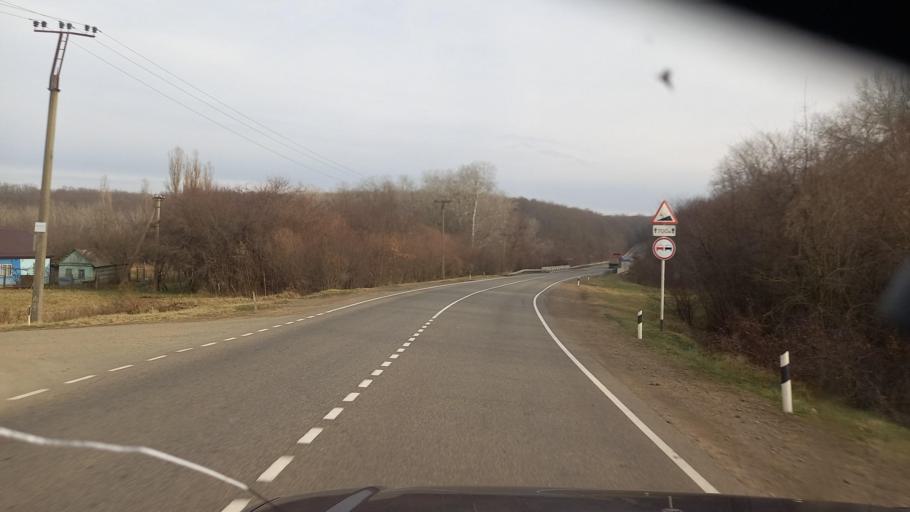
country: RU
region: Krasnodarskiy
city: Saratovskaya
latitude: 44.6945
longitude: 39.3674
